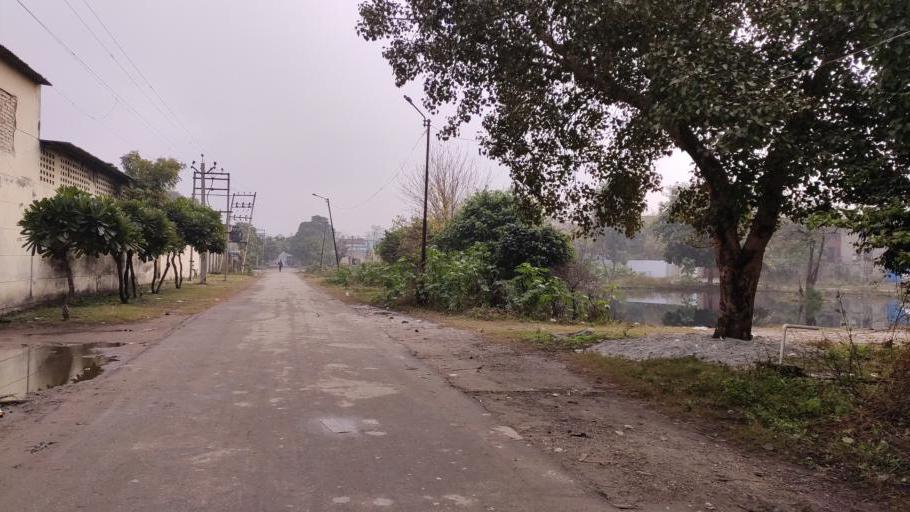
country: IN
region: Punjab
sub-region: Amritsar
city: Amritsar
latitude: 31.6234
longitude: 74.9197
